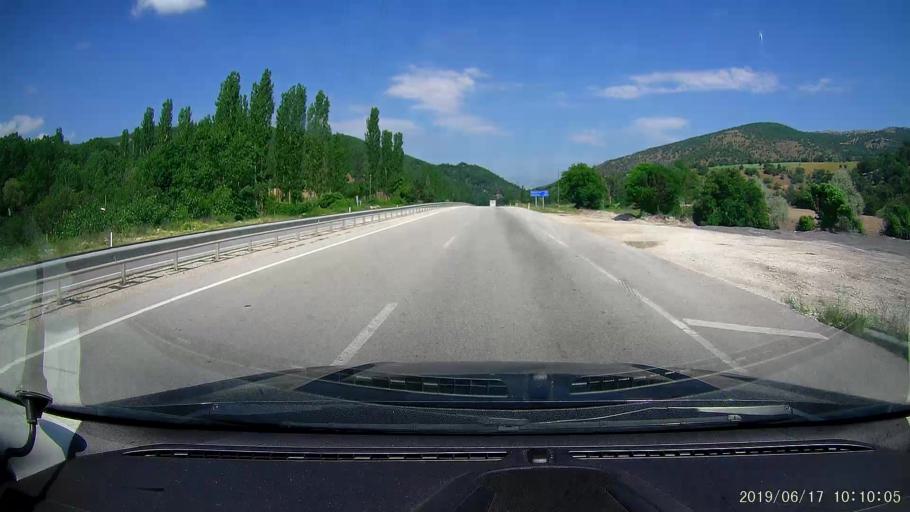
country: TR
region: Amasya
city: Saraycik
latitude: 40.9565
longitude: 35.1073
